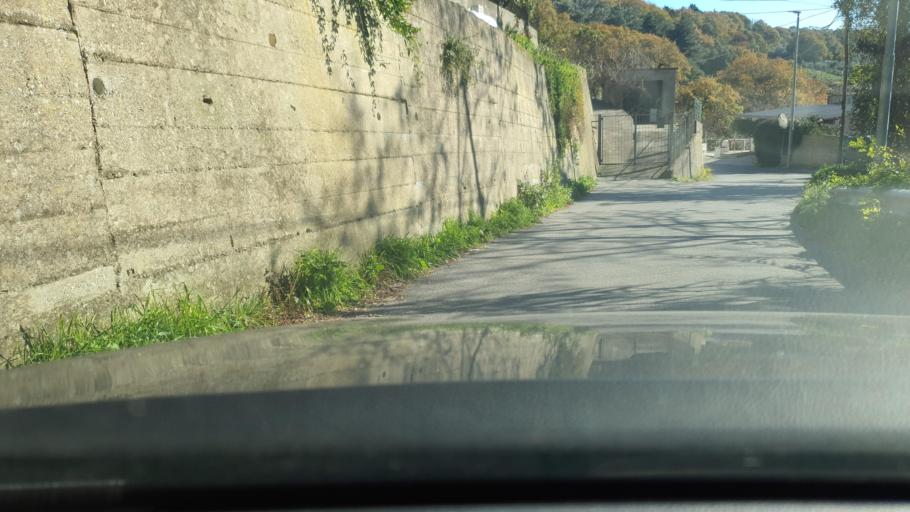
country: IT
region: Calabria
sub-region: Provincia di Catanzaro
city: Sant'Elia
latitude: 38.9568
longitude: 16.5806
